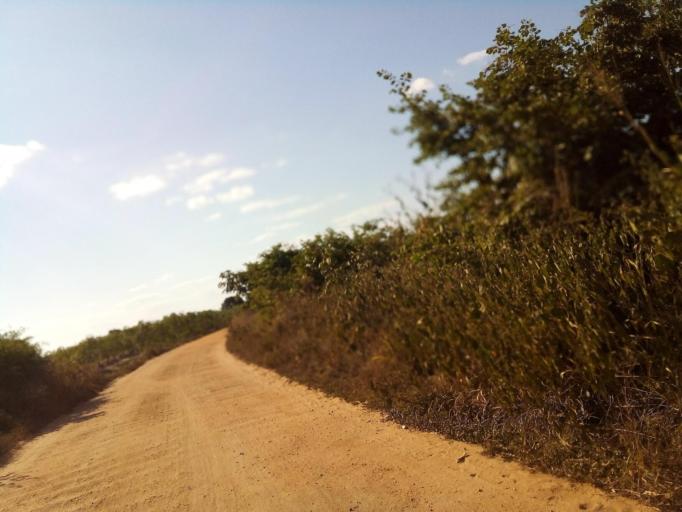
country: MZ
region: Zambezia
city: Quelimane
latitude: -17.5633
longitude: 36.6360
